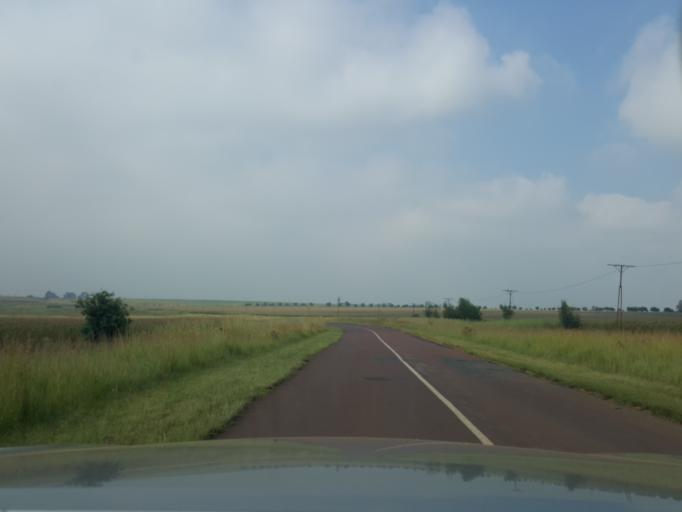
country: ZA
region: Mpumalanga
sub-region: Nkangala District Municipality
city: Middelburg
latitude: -25.9905
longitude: 29.4524
